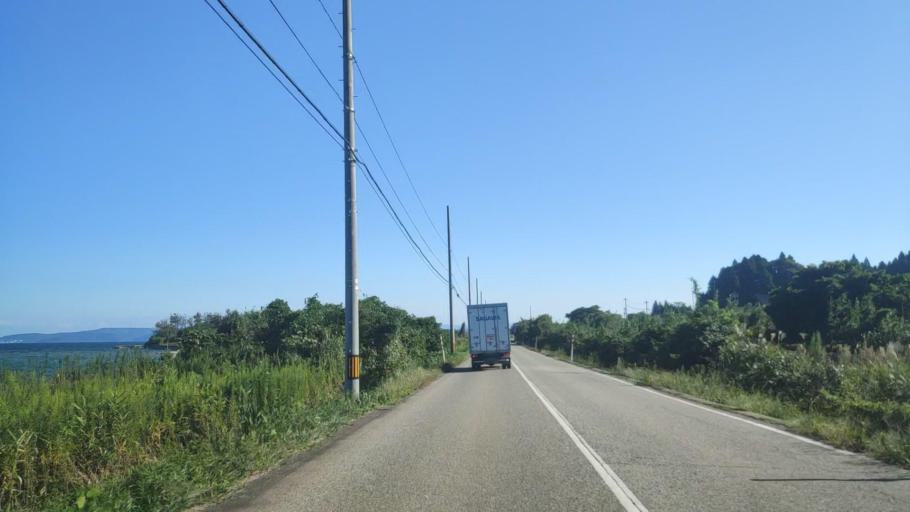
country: JP
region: Ishikawa
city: Nanao
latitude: 37.1970
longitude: 136.9102
